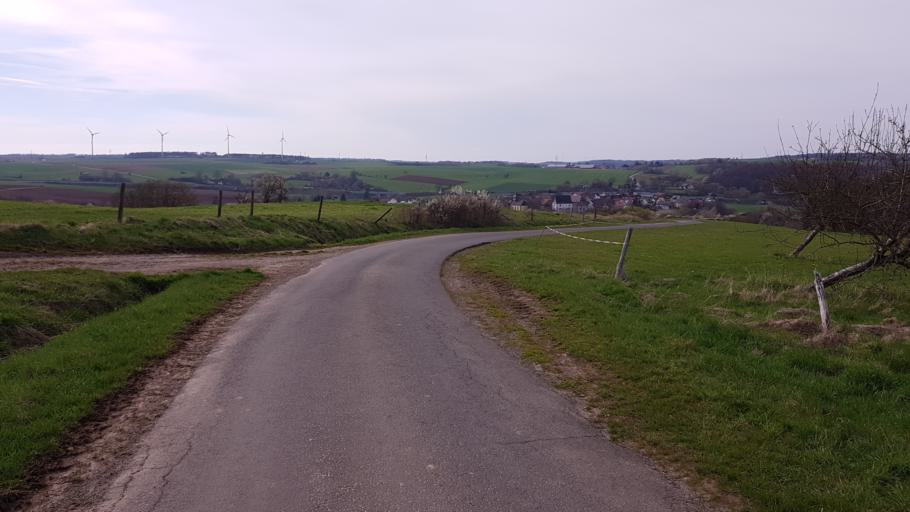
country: DE
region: Hesse
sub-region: Regierungsbezirk Giessen
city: Homberg
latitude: 50.6775
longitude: 9.0481
